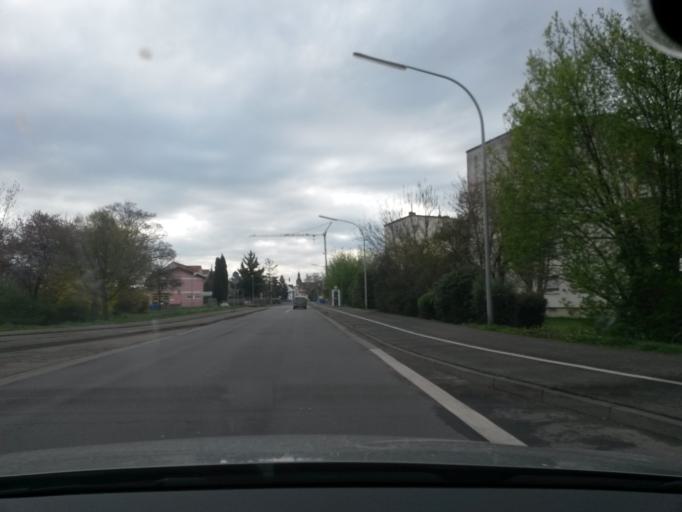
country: DE
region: Rheinland-Pfalz
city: Worms
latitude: 49.6478
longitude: 8.3455
